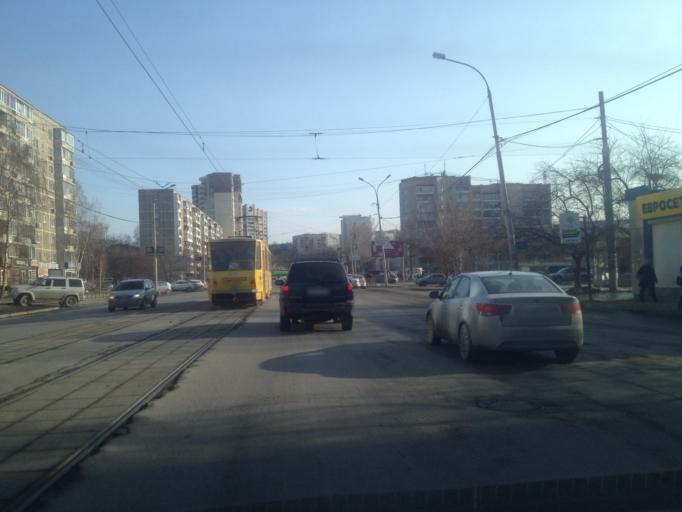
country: RU
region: Sverdlovsk
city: Yekaterinburg
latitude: 56.8215
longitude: 60.5692
